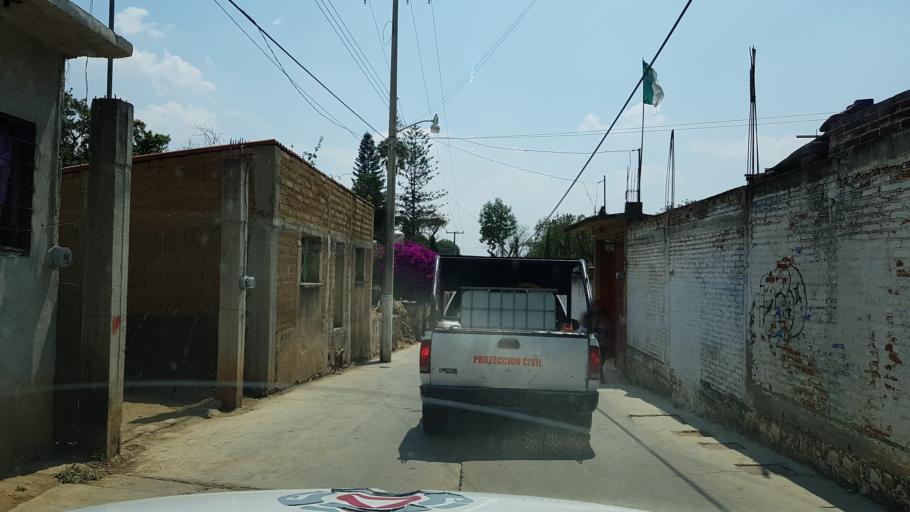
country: MX
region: Morelos
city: Ocuituco
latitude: 18.8840
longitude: -98.8174
